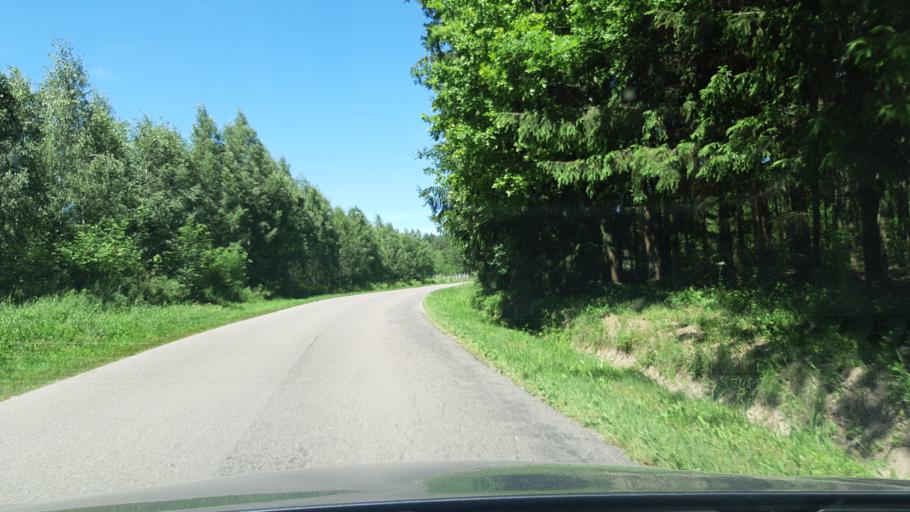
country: PL
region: Warmian-Masurian Voivodeship
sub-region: Powiat gizycki
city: Gizycko
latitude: 53.9554
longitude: 21.7598
